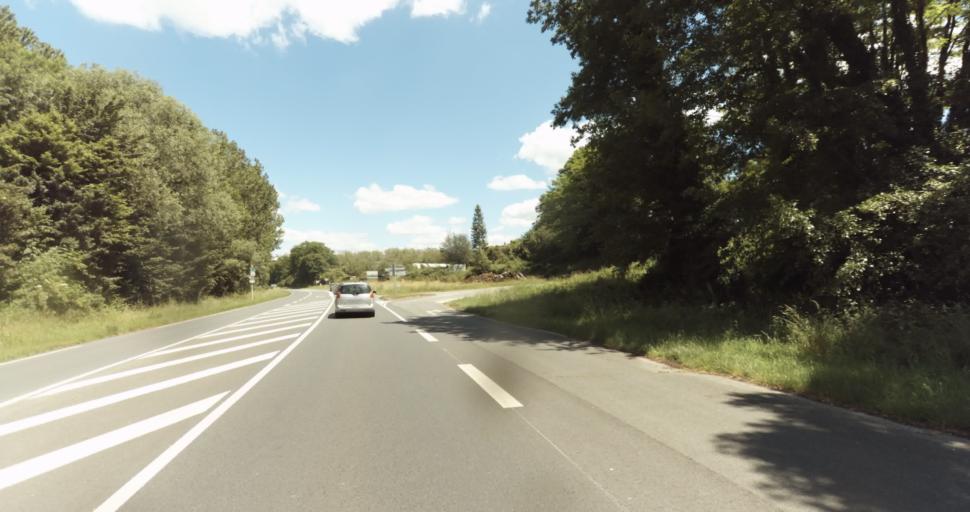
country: FR
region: Aquitaine
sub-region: Departement de la Dordogne
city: Belves
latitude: 44.8213
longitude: 0.9660
